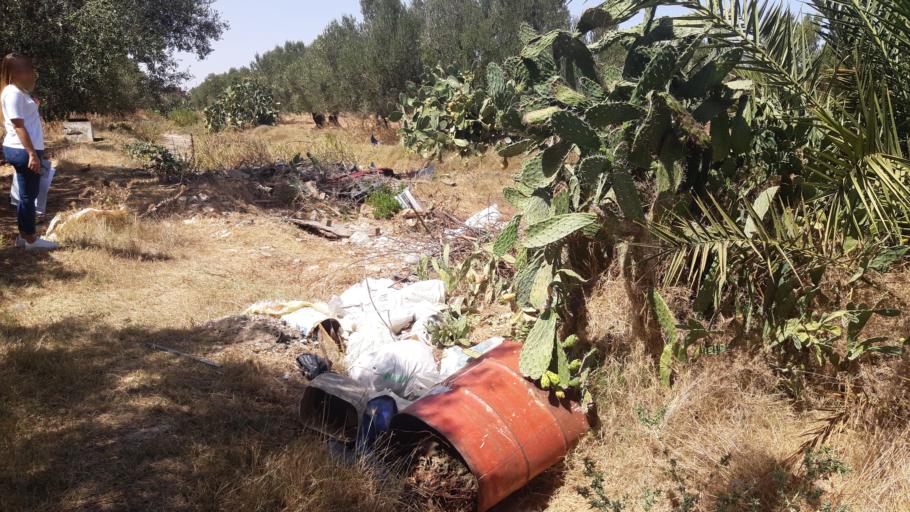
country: TN
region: Al Munastir
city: Qusaybat al Madyuni
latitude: 35.6774
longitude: 10.8597
